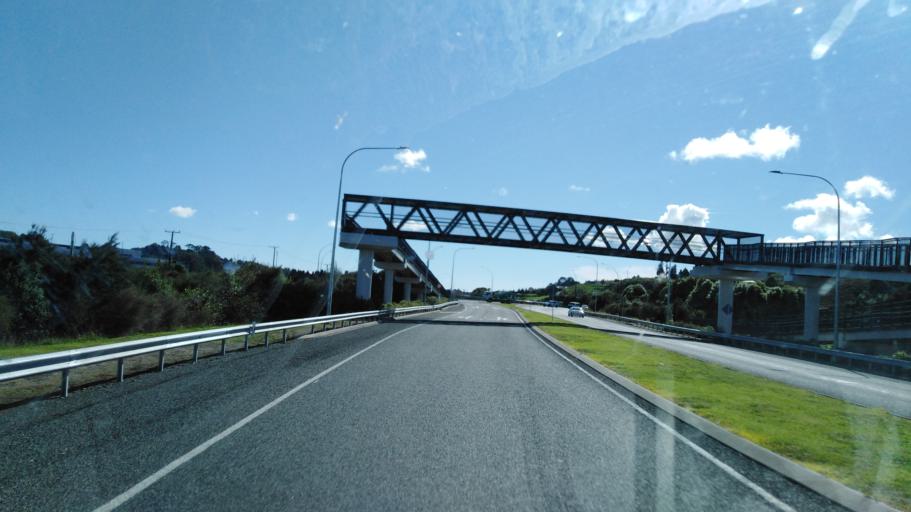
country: NZ
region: Bay of Plenty
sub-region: Tauranga City
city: Tauranga
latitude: -37.7401
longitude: 176.1069
